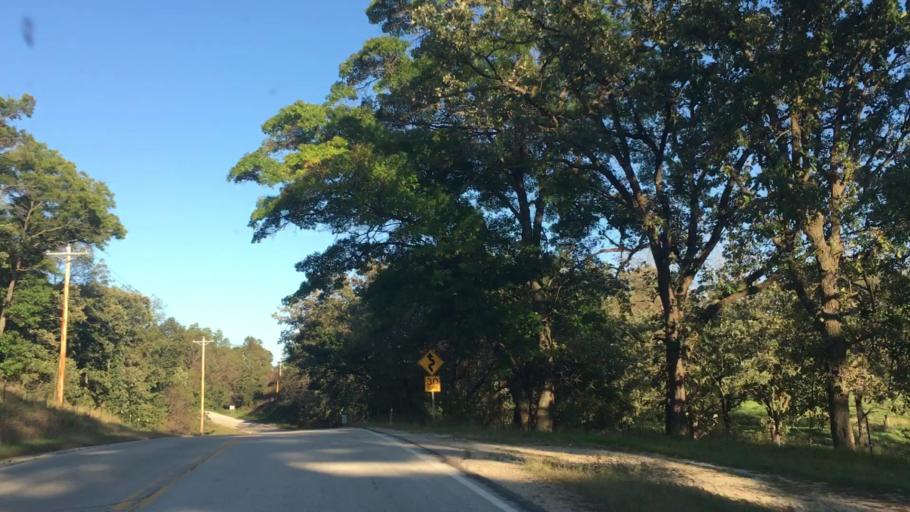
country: US
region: Minnesota
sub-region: Fillmore County
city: Chatfield
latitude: 43.8180
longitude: -92.0438
